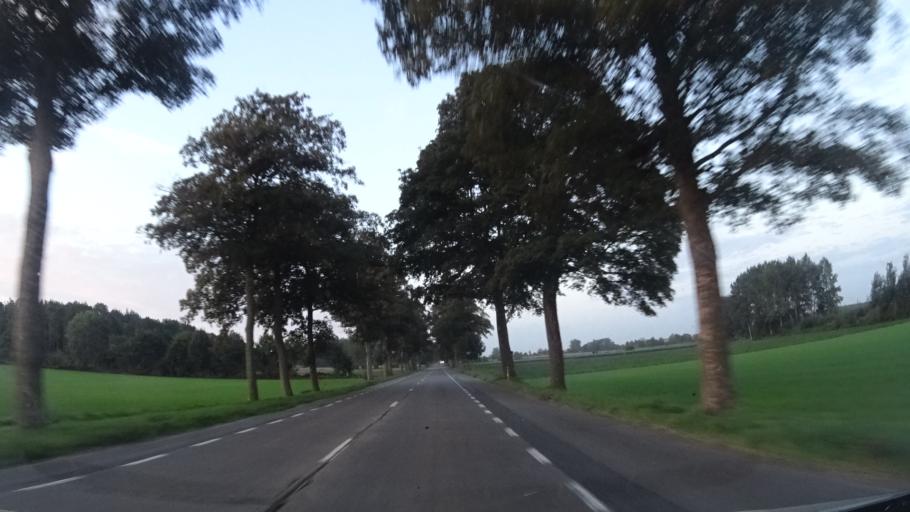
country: BE
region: Wallonia
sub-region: Province du Hainaut
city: Peruwelz
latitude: 50.5568
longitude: 3.6095
